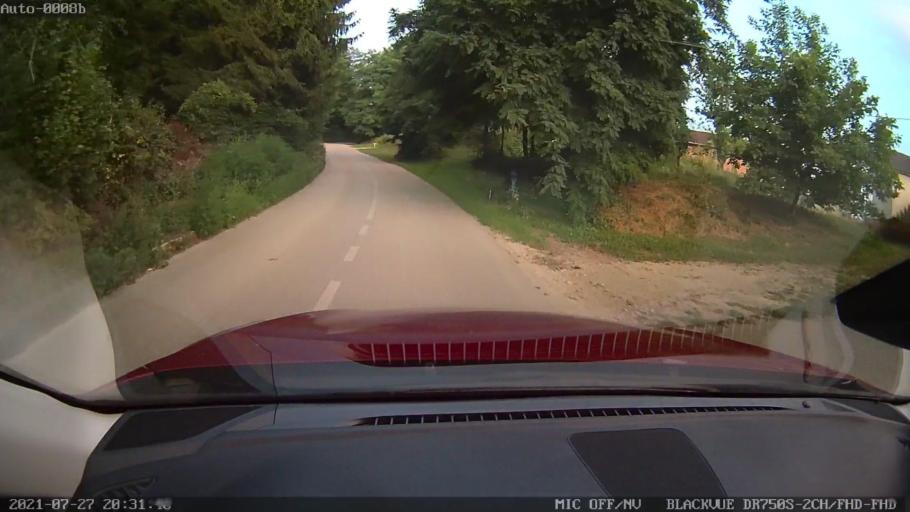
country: HR
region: Varazdinska
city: Jalzabet
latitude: 46.2462
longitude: 16.4731
